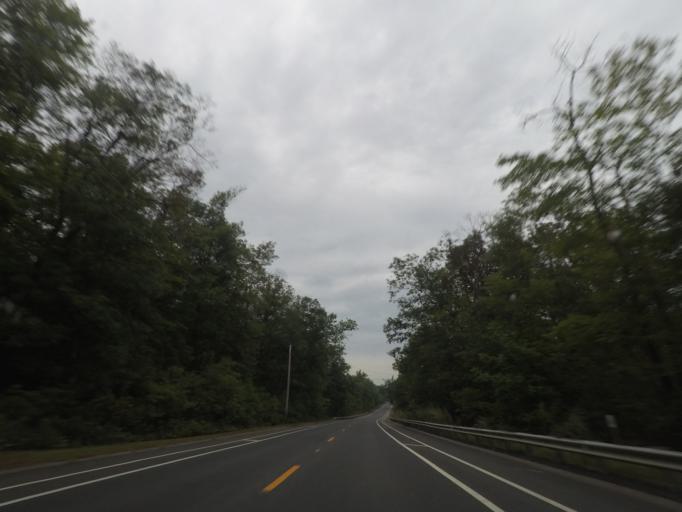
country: US
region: Massachusetts
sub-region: Hampden County
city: Palmer
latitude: 42.1807
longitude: -72.2644
